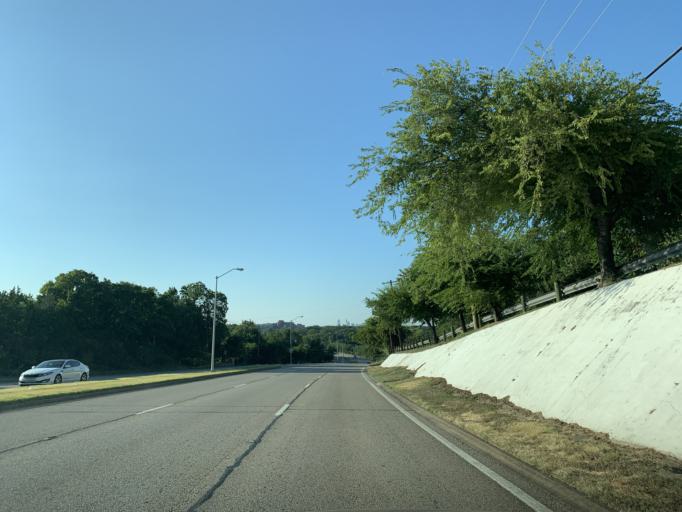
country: US
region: Texas
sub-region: Dallas County
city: Hutchins
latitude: 32.6746
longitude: -96.7847
